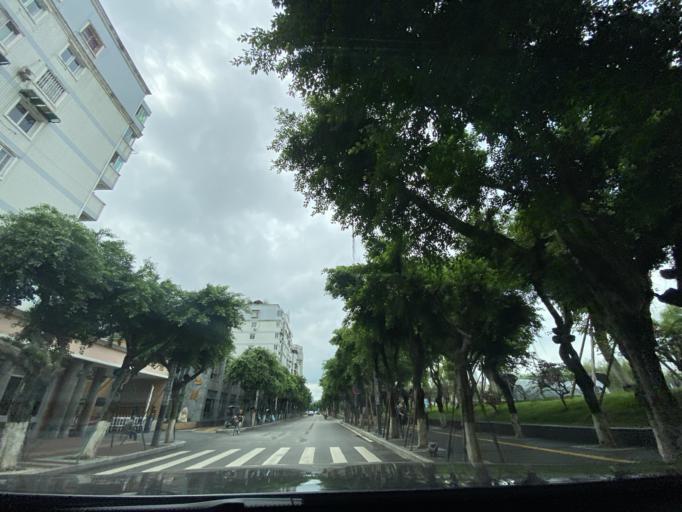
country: CN
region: Sichuan
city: Jiancheng
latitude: 30.3940
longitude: 104.5539
